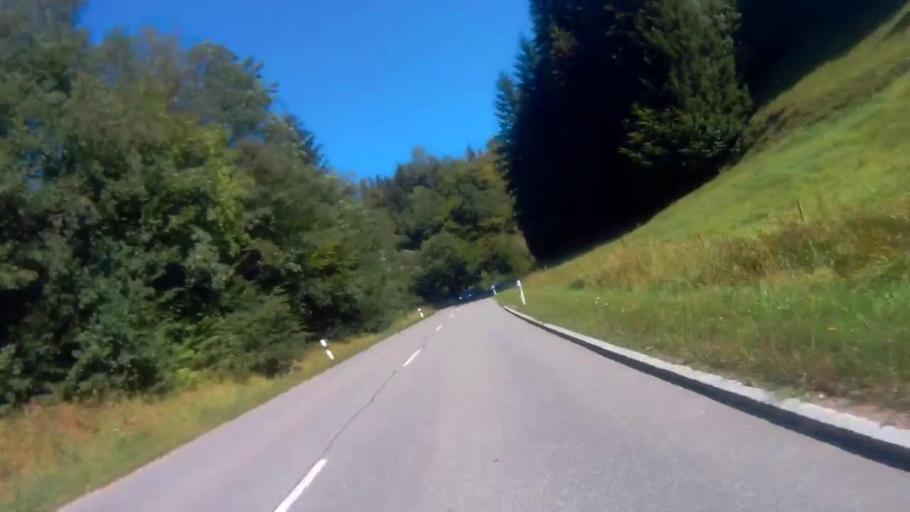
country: DE
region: Baden-Wuerttemberg
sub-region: Freiburg Region
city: Hausen
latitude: 47.7147
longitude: 7.7942
